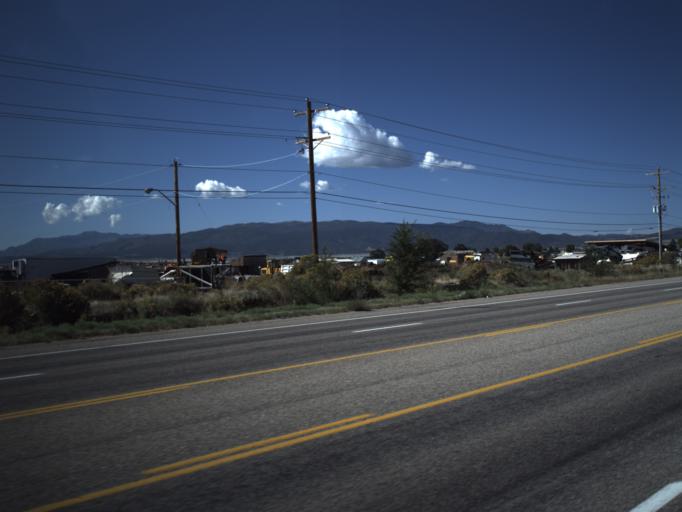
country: US
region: Utah
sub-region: Iron County
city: Cedar City
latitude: 37.6851
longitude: -113.1174
